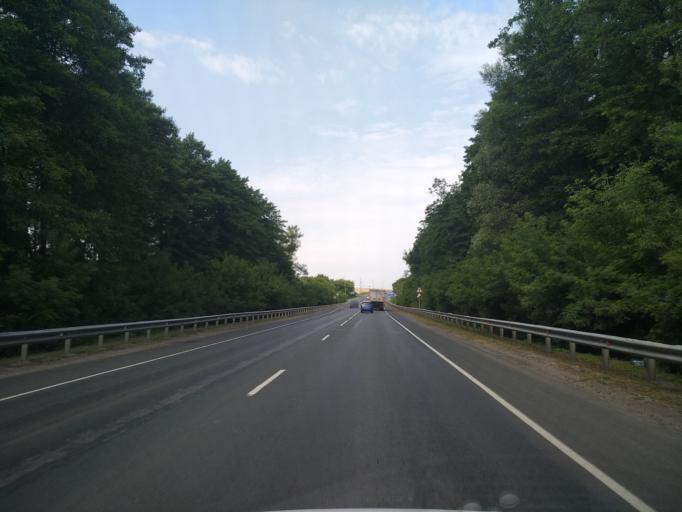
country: RU
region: Voronezj
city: Orlovo
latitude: 51.6816
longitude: 39.5775
